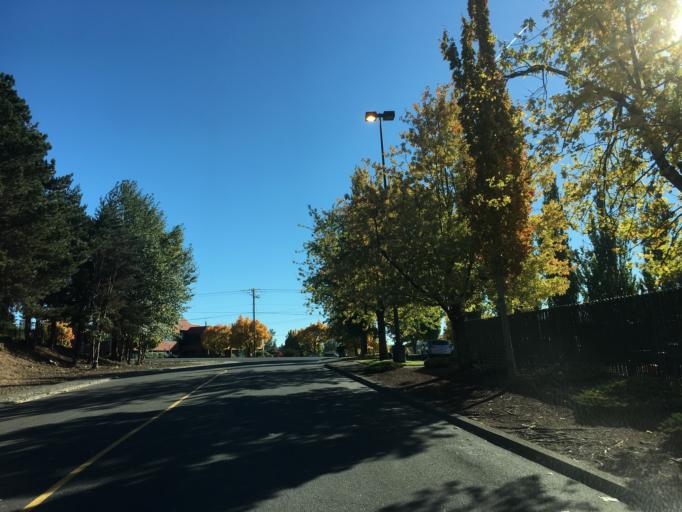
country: US
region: Oregon
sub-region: Multnomah County
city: Gresham
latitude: 45.4941
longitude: -122.4039
